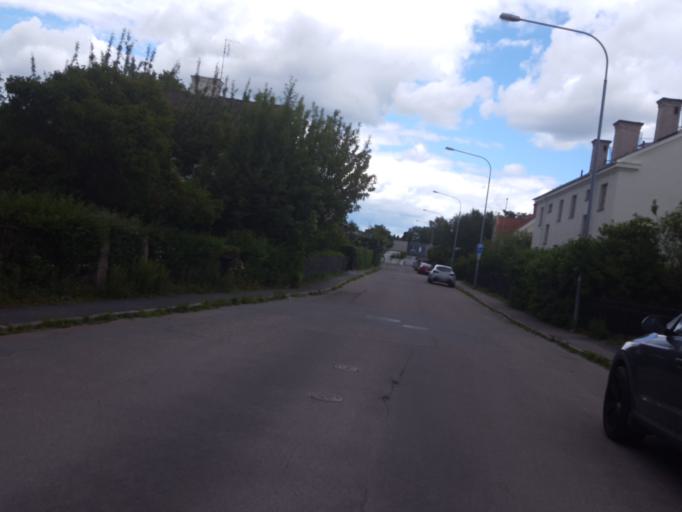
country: SE
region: Uppsala
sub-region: Uppsala Kommun
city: Uppsala
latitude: 59.8604
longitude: 17.6581
